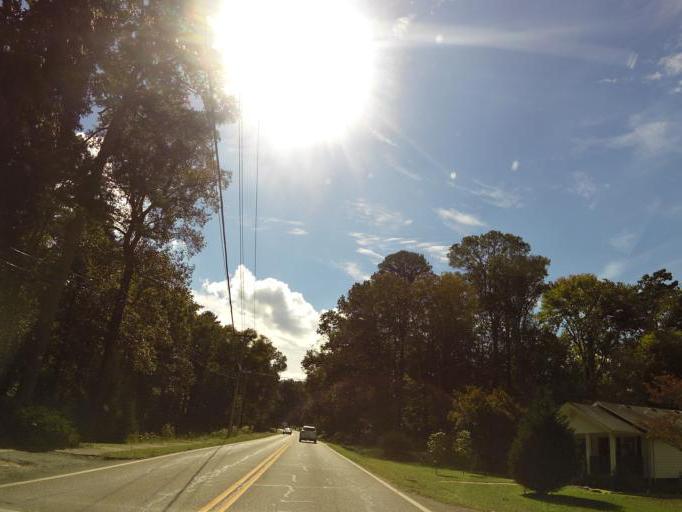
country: US
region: Georgia
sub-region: Pickens County
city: Nelson
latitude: 34.4182
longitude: -84.3836
